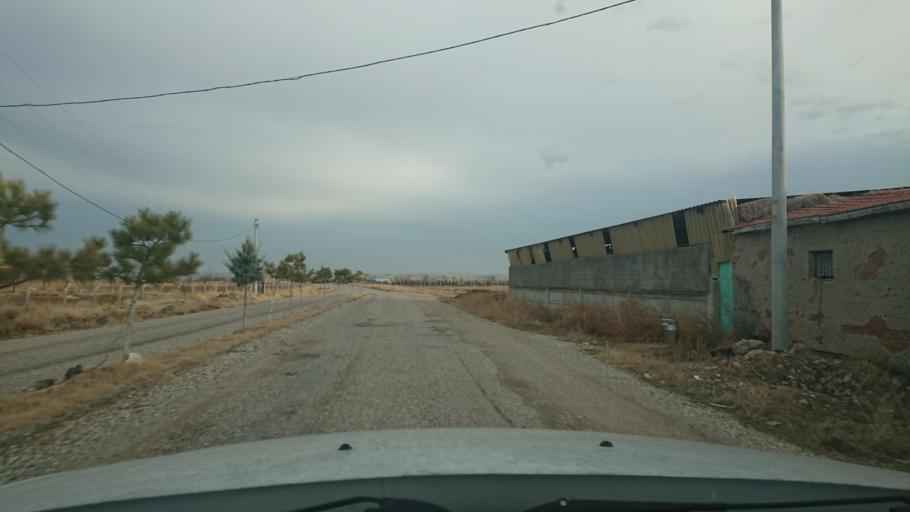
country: TR
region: Aksaray
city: Yesilova
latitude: 38.4240
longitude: 33.8345
